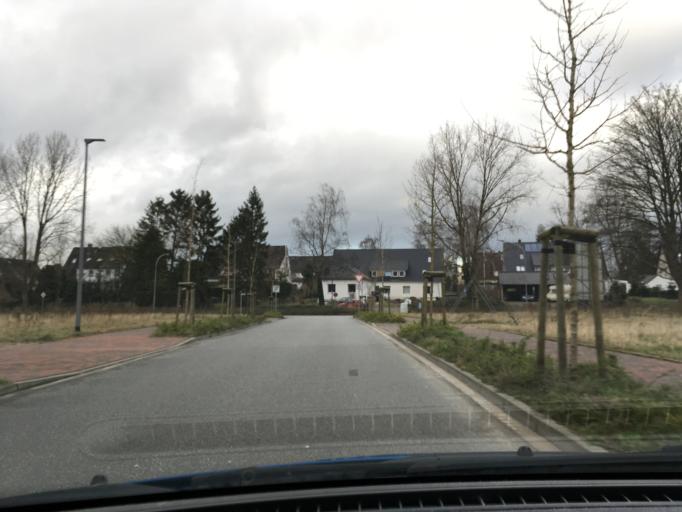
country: DE
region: Schleswig-Holstein
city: Kremperheide
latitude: 53.9000
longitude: 9.4976
